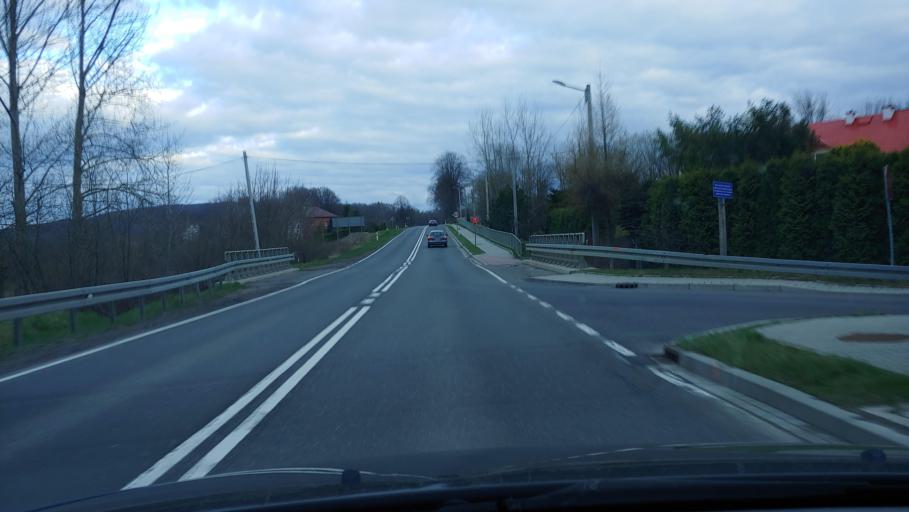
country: PL
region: Lesser Poland Voivodeship
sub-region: Powiat krakowski
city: Rudawa
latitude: 50.1181
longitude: 19.6940
